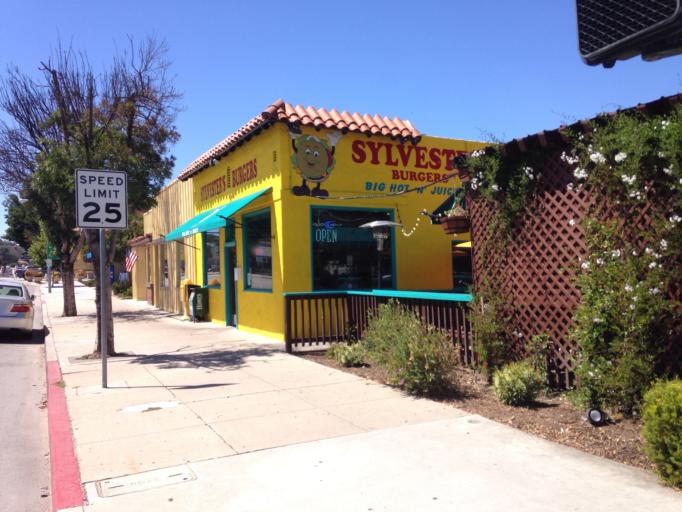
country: US
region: California
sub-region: San Luis Obispo County
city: Atascadero
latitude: 35.4886
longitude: -120.6686
